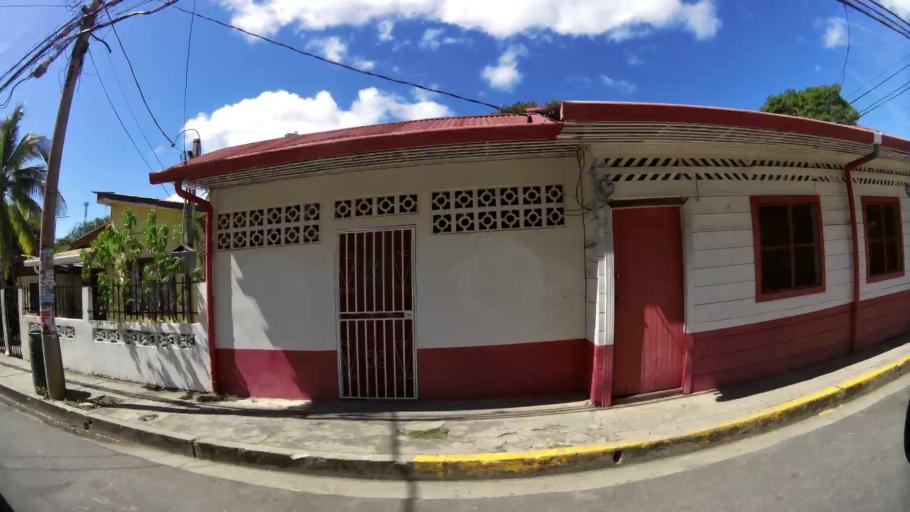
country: CR
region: Guanacaste
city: Bagaces
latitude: 10.5253
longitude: -85.2555
